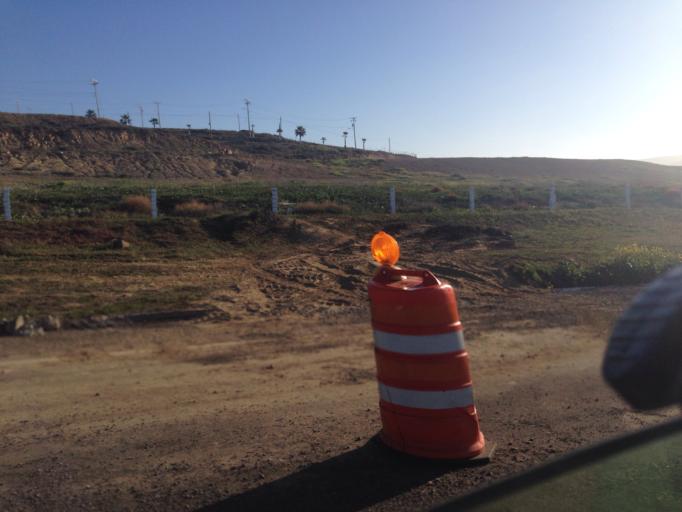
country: MX
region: Baja California
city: Primo Tapia
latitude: 32.2366
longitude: -116.9266
